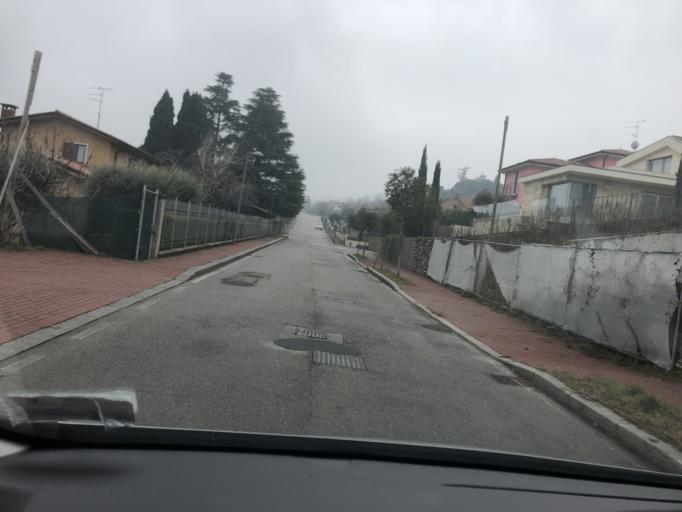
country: IT
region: Veneto
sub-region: Provincia di Verona
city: Sona
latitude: 45.4342
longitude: 10.8375
